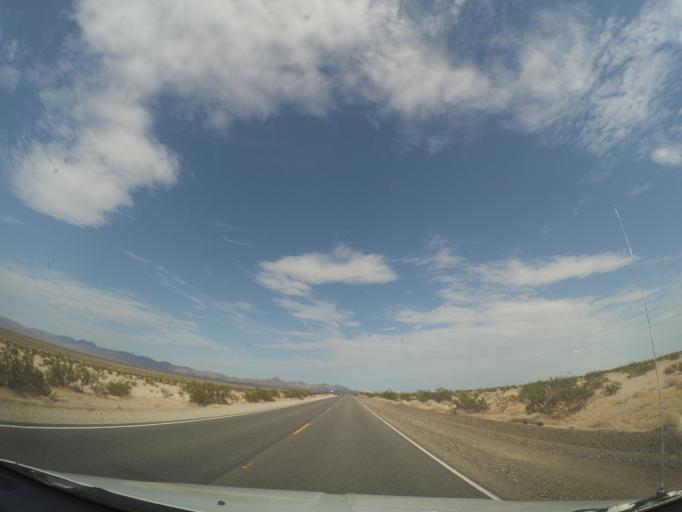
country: US
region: California
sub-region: Riverside County
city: Mesa Verde
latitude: 34.1052
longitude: -114.9566
